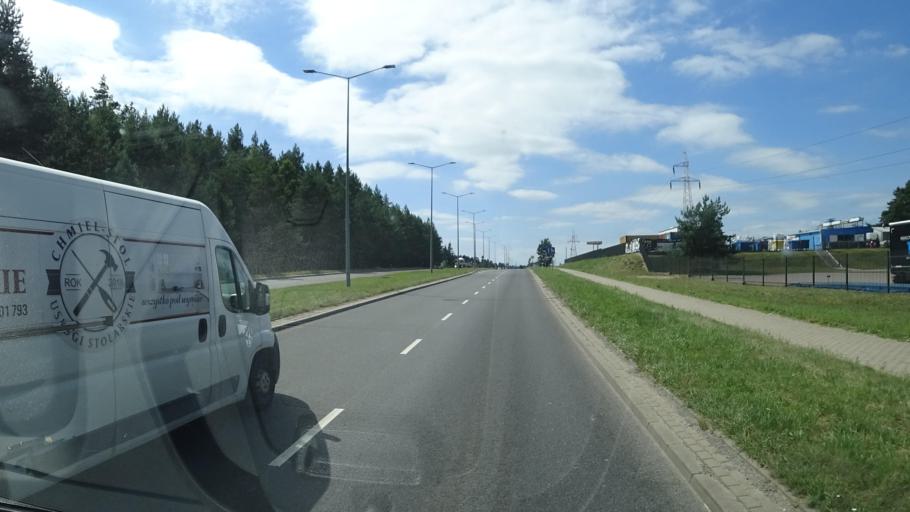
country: PL
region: Warmian-Masurian Voivodeship
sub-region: Powiat elcki
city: Elk
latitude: 53.8165
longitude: 22.3859
